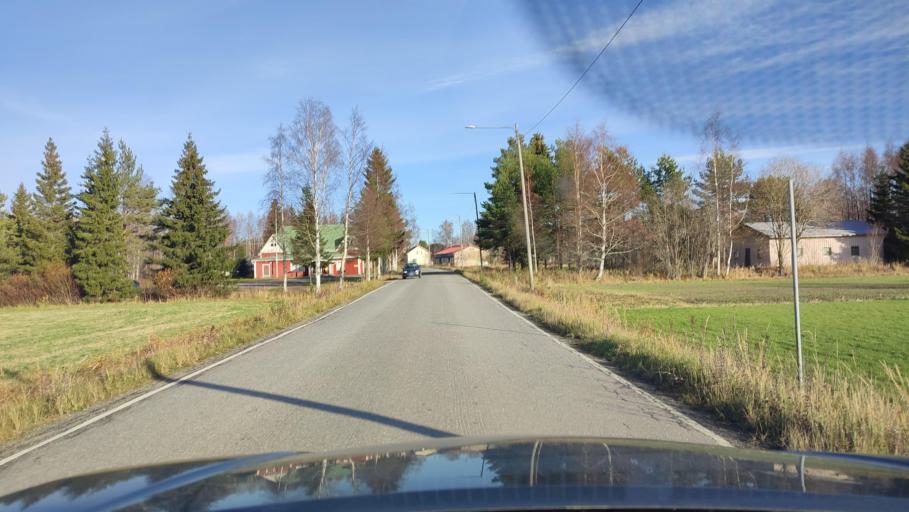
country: FI
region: Southern Ostrobothnia
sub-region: Suupohja
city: Teuva
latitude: 62.4520
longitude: 21.6016
